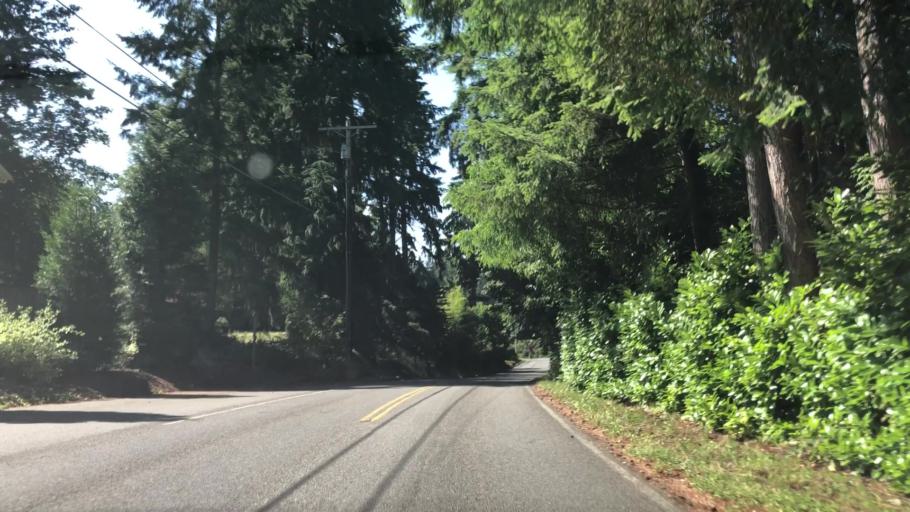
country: US
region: Washington
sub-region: Snohomish County
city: Alderwood Manor
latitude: 47.8202
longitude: -122.2525
